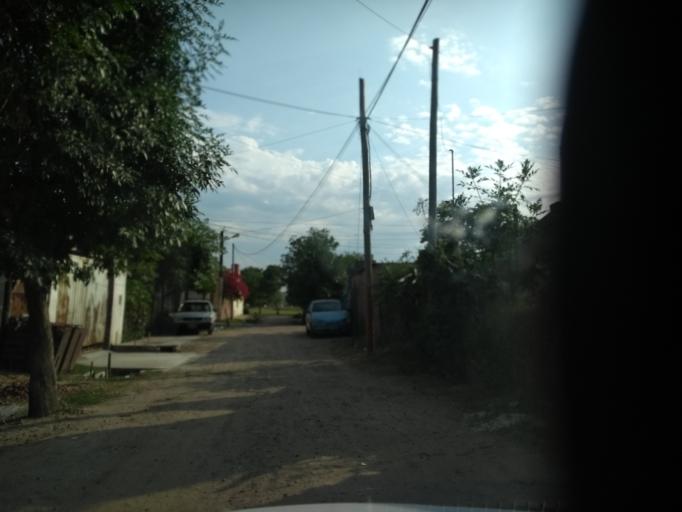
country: AR
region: Chaco
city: Resistencia
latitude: -27.4709
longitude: -58.9743
